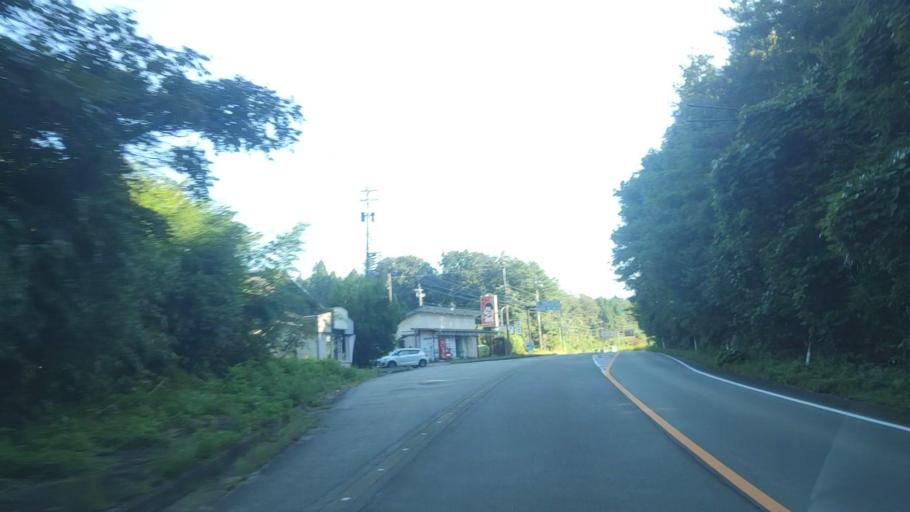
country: JP
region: Ishikawa
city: Nanao
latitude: 37.1320
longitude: 136.8638
